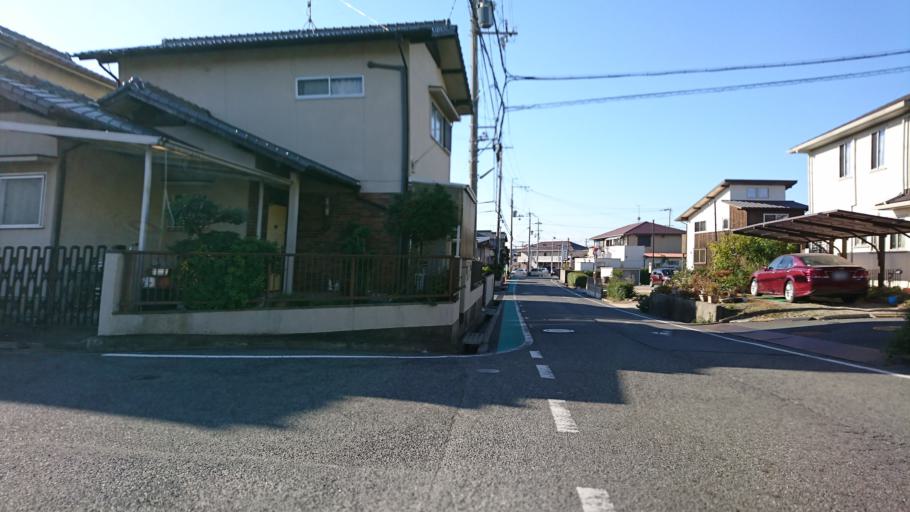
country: JP
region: Hyogo
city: Kakogawacho-honmachi
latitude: 34.7482
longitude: 134.8517
